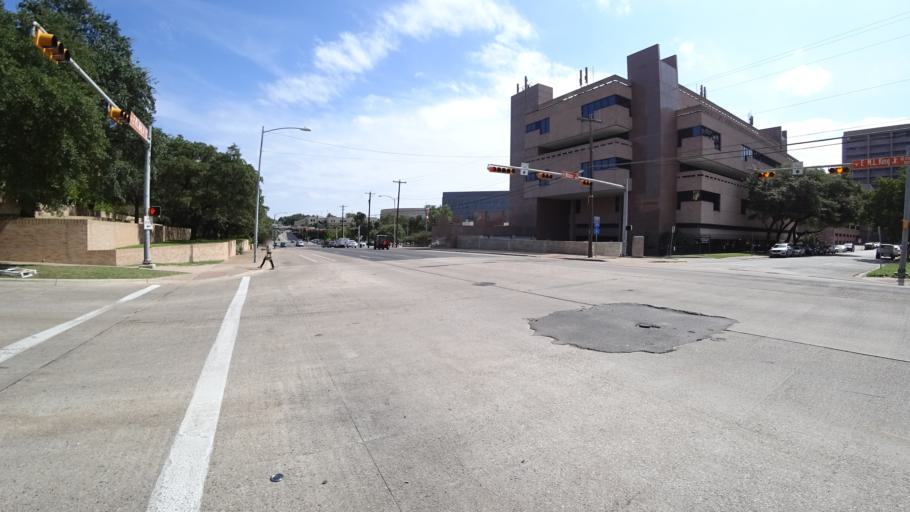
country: US
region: Texas
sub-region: Travis County
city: Austin
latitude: 30.2804
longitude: -97.7369
